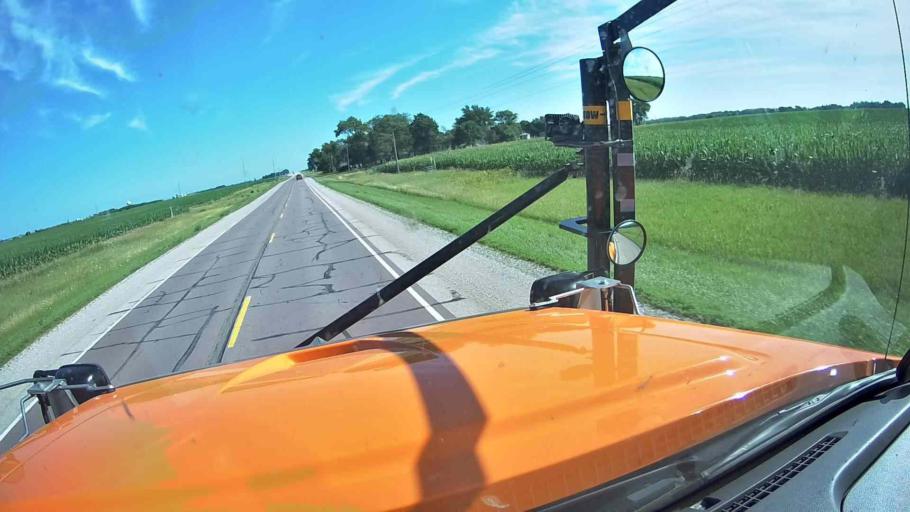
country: US
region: Iowa
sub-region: Cerro Gordo County
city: Mason City
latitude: 43.0923
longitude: -93.2014
